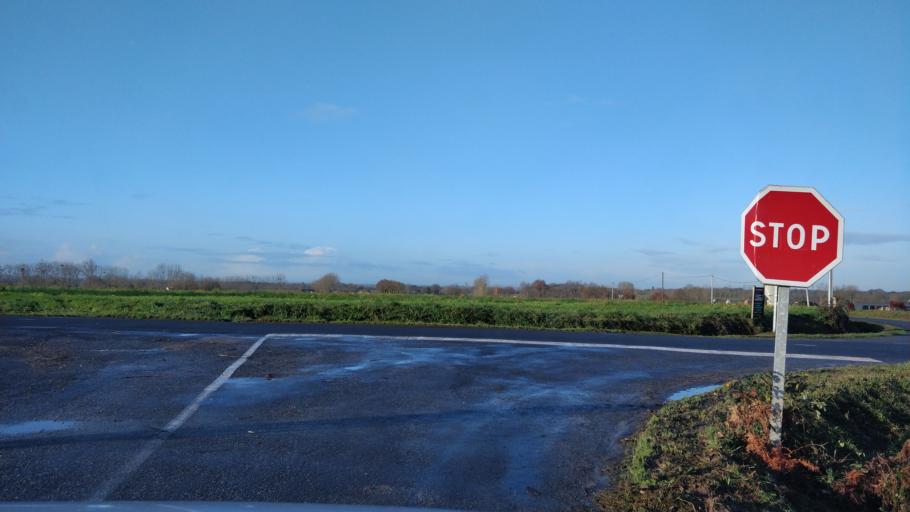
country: FR
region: Brittany
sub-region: Departement d'Ille-et-Vilaine
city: Chavagne
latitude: 48.0670
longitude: -1.7917
